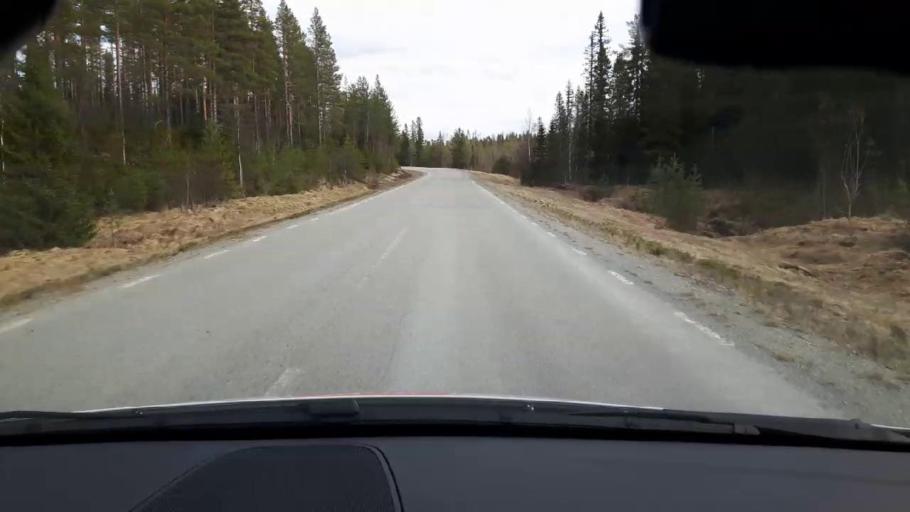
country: SE
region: Jaemtland
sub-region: Bergs Kommun
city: Hoverberg
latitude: 62.6839
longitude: 14.6415
